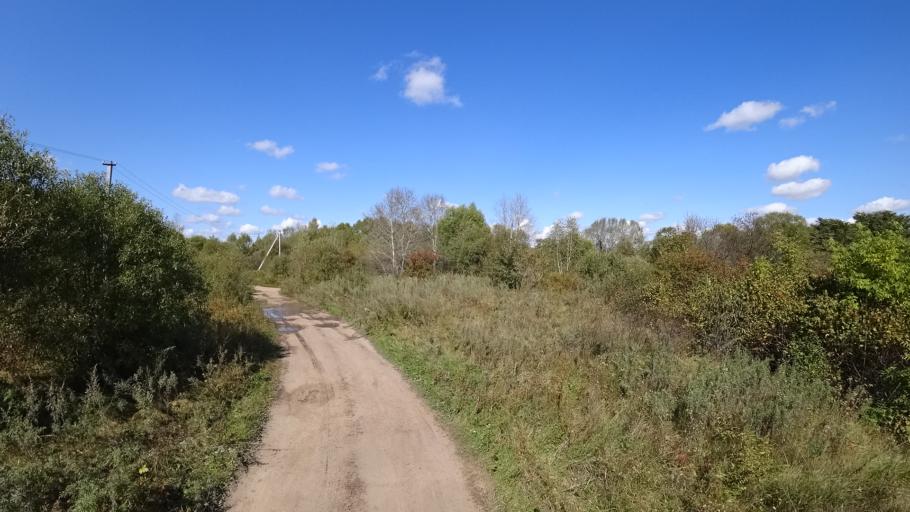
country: RU
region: Amur
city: Arkhara
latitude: 49.3993
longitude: 130.1305
